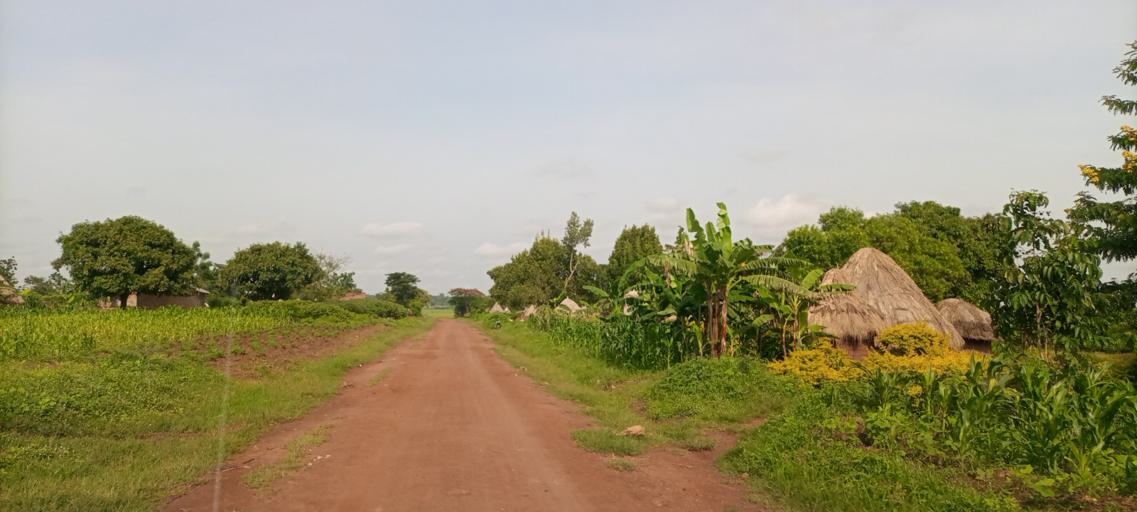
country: UG
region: Eastern Region
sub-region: Kibuku District
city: Kibuku
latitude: 1.1036
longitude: 33.7812
